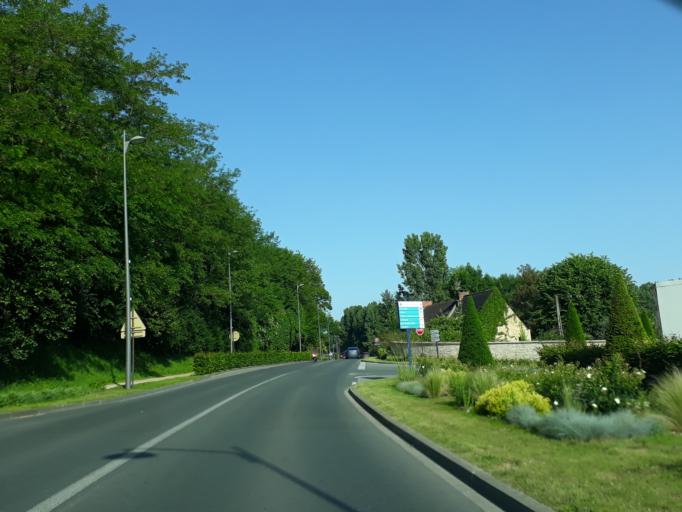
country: FR
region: Aquitaine
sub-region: Departement de la Dordogne
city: Terrasson-Lavilledieu
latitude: 45.1287
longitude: 1.3154
